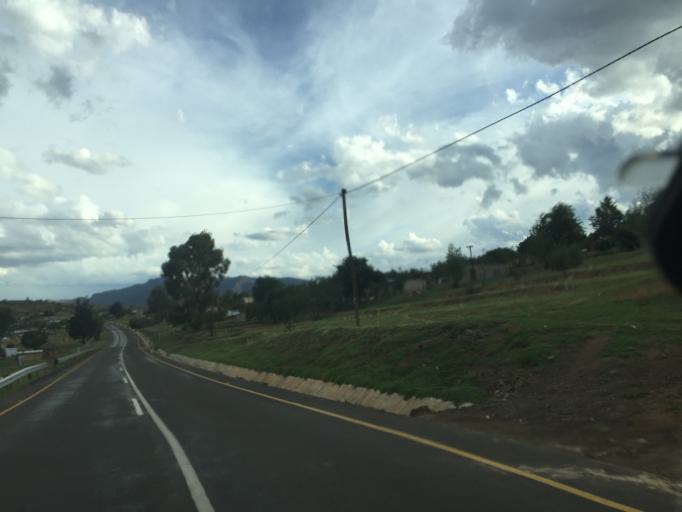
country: LS
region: Berea
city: Teyateyaneng
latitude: -29.1291
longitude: 27.9845
